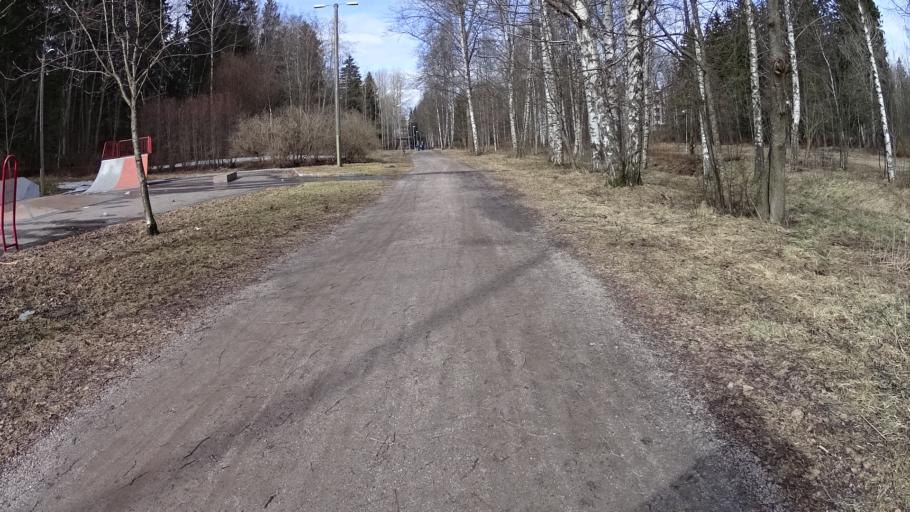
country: FI
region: Uusimaa
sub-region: Helsinki
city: Teekkarikylae
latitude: 60.2259
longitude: 24.8859
